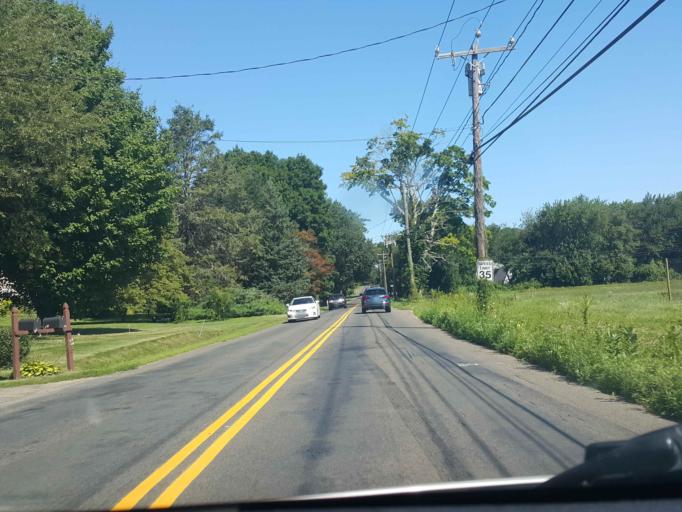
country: US
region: Connecticut
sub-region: New Haven County
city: Guilford
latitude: 41.2985
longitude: -72.6967
